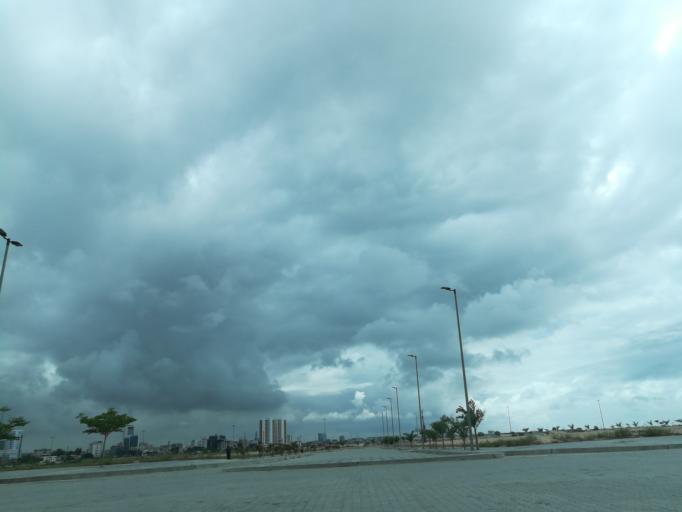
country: NG
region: Lagos
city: Ikoyi
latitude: 6.4152
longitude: 3.4154
